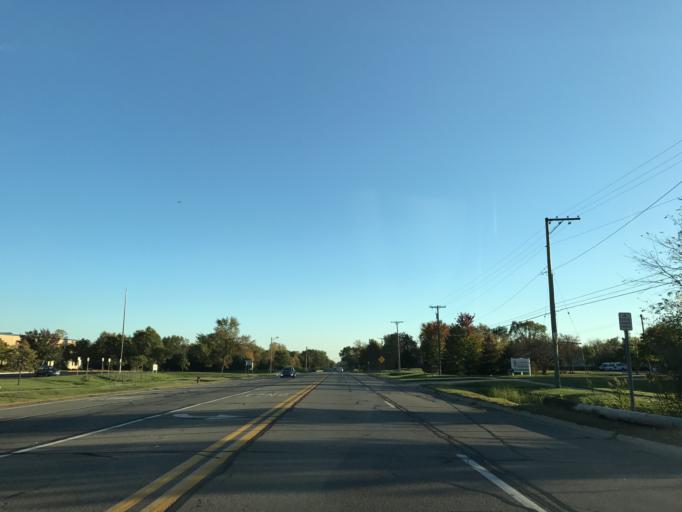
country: US
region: Michigan
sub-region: Oakland County
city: Farmington Hills
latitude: 42.4799
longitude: -83.3382
